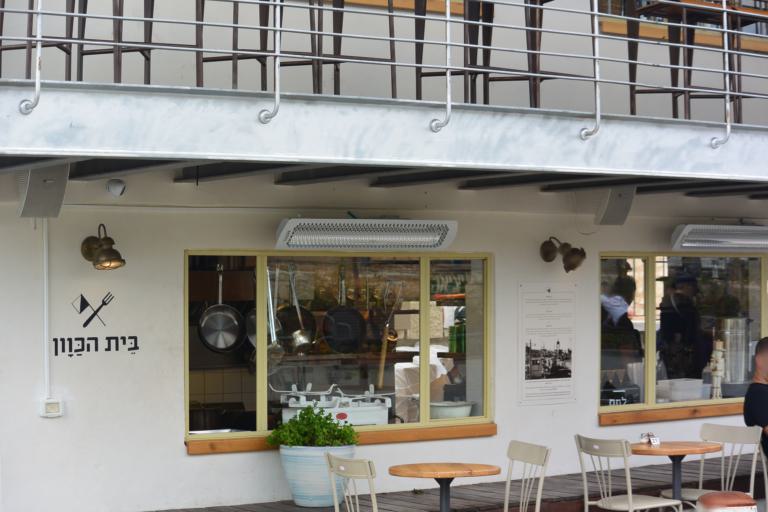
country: IL
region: Jerusalem
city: Jerusalem
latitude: 31.7646
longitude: 35.2246
